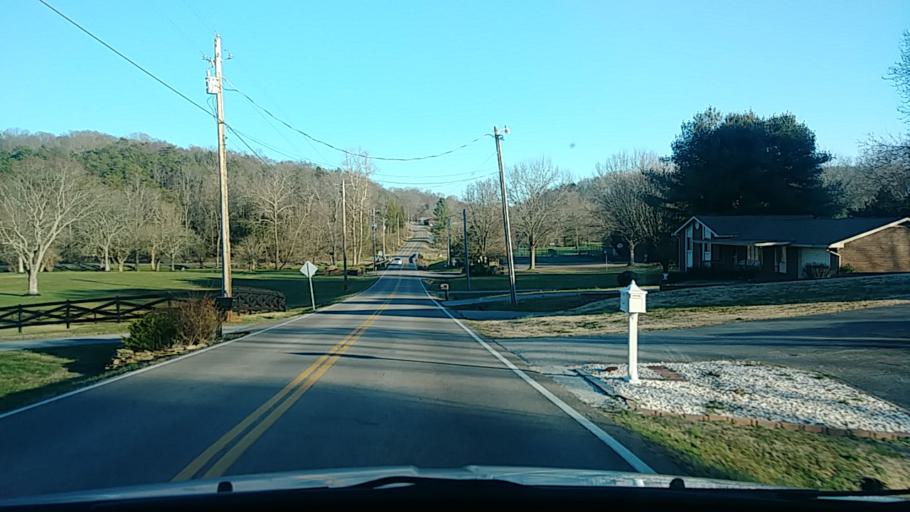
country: US
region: Tennessee
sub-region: Hamblen County
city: Morristown
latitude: 36.1967
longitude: -83.3972
